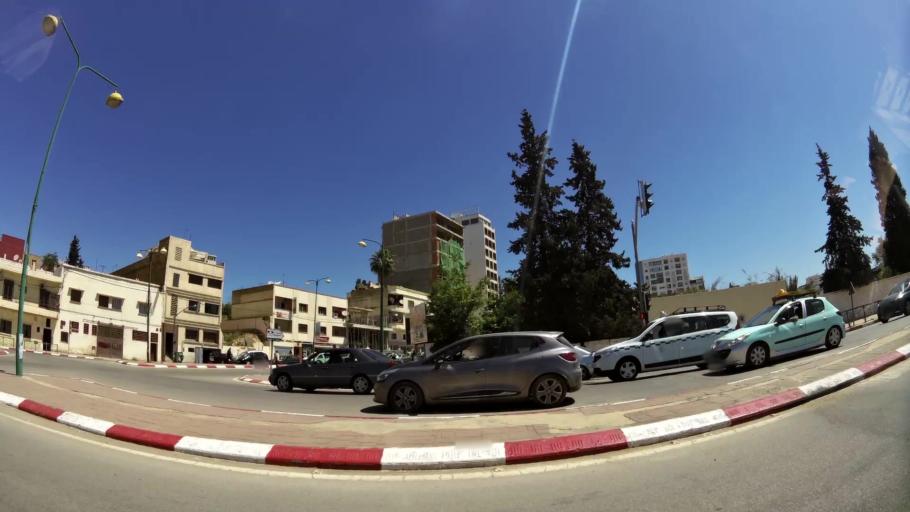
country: MA
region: Meknes-Tafilalet
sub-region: Meknes
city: Meknes
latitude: 33.8942
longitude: -5.5496
